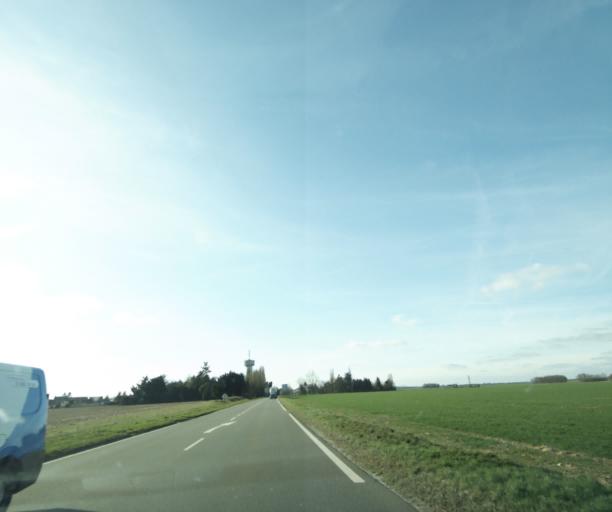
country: FR
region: Ile-de-France
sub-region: Departement des Yvelines
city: Ablis
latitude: 48.4635
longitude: 1.8822
